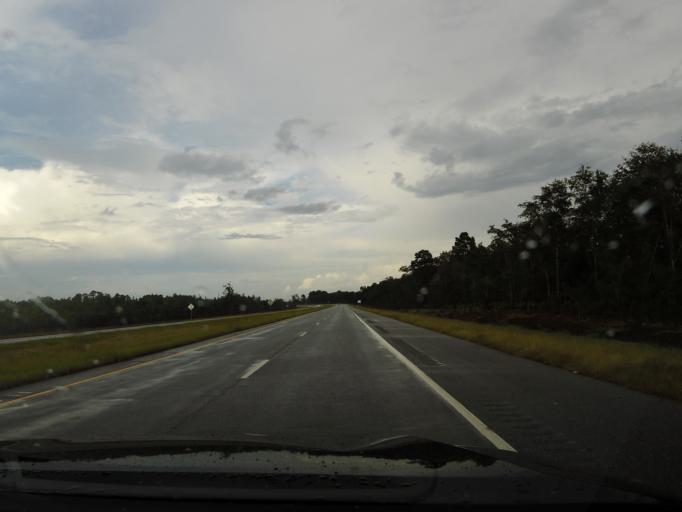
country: US
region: Georgia
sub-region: Wayne County
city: Jesup
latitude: 31.6018
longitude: -81.8641
